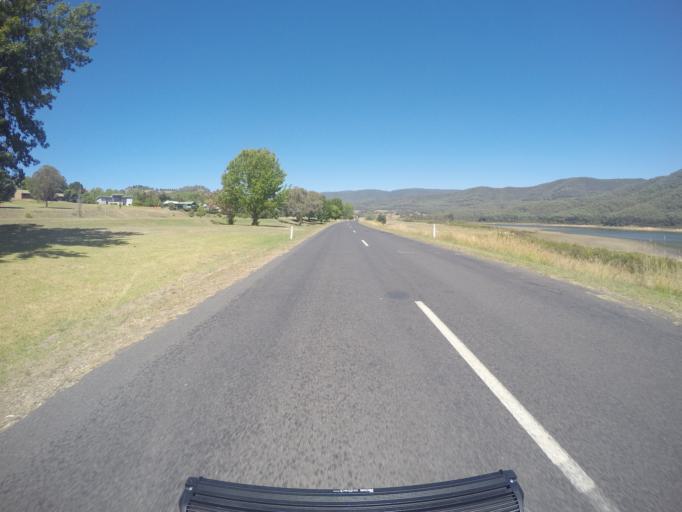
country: AU
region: New South Wales
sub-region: Tumut Shire
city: Tumut
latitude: -35.5815
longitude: 148.2962
